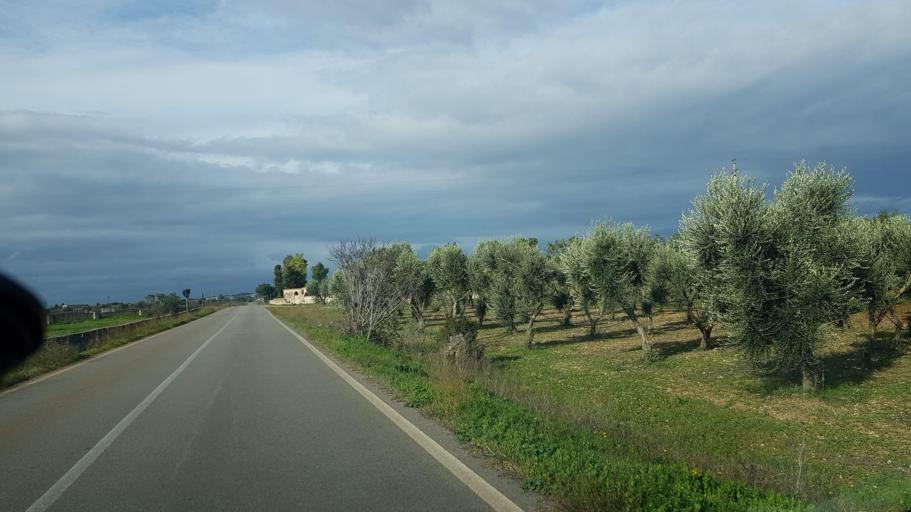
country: IT
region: Apulia
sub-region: Provincia di Brindisi
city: Torre Santa Susanna
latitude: 40.4782
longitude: 17.6951
